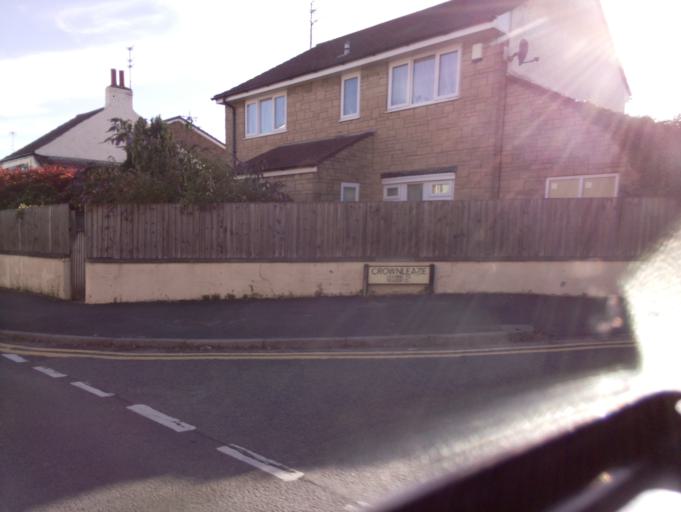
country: GB
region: England
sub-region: South Gloucestershire
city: Mangotsfield
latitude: 51.4761
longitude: -2.5080
